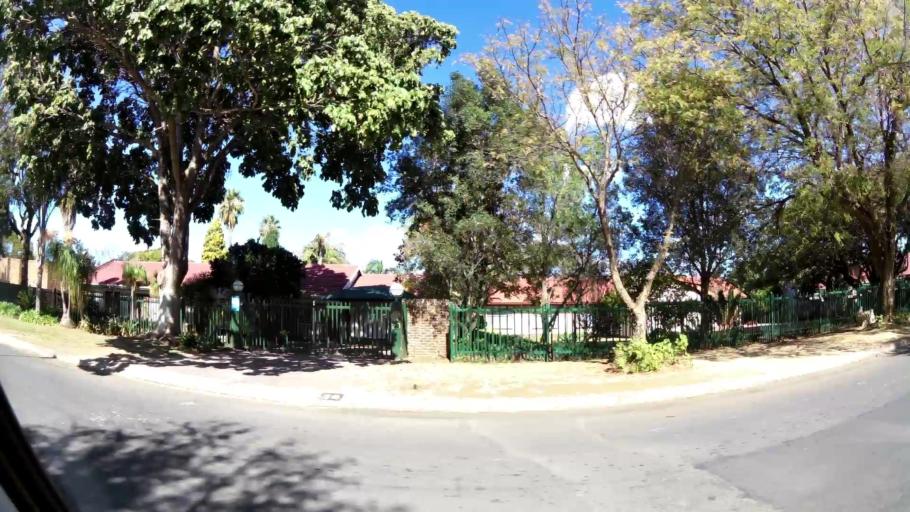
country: ZA
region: Limpopo
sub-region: Capricorn District Municipality
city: Polokwane
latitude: -23.9002
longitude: 29.4856
